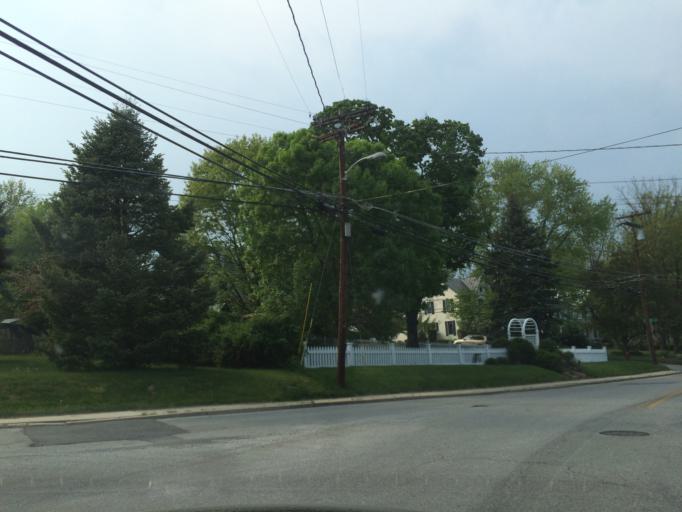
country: US
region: Maryland
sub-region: Carroll County
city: Mount Airy
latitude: 39.3722
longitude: -77.1539
